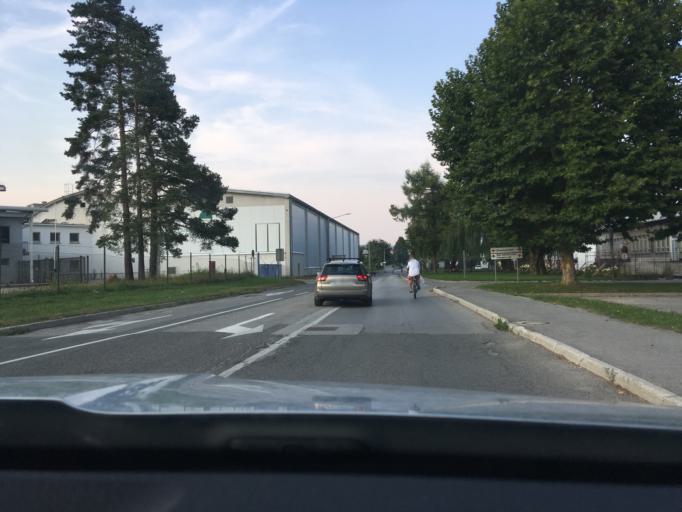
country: SI
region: Kocevje
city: Kocevje
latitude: 45.6395
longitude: 14.8648
